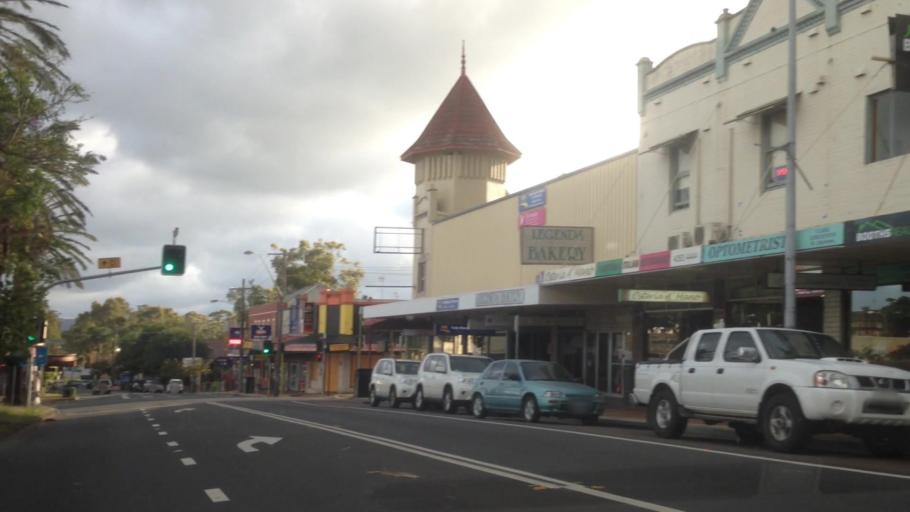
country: AU
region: New South Wales
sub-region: Wyong Shire
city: Chittaway Bay
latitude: -33.2853
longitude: 151.4247
